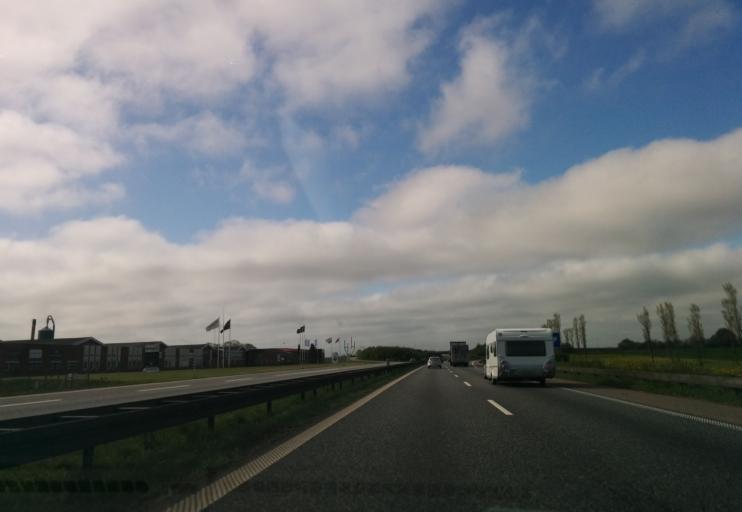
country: DK
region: Central Jutland
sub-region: Hedensted Kommune
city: Hedensted
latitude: 55.7959
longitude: 9.6719
